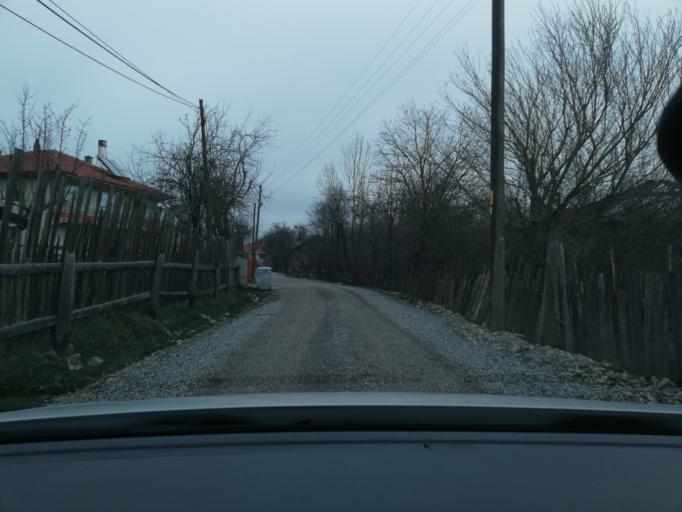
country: TR
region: Bolu
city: Bolu
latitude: 40.6632
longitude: 31.4606
